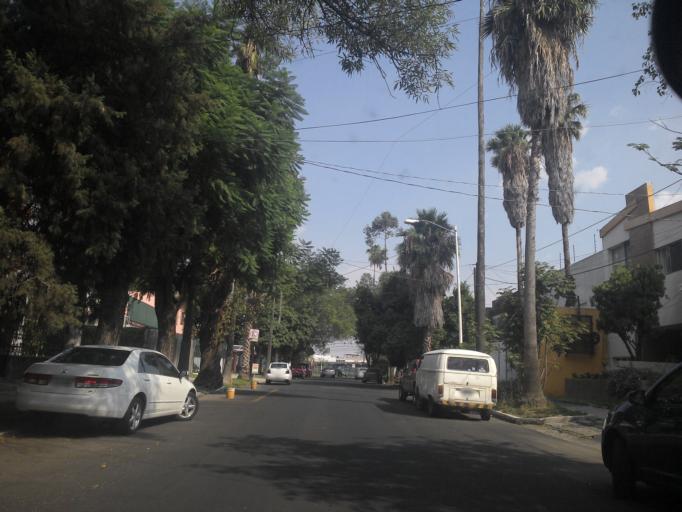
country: MX
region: Jalisco
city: Guadalajara
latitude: 20.6616
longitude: -103.3603
